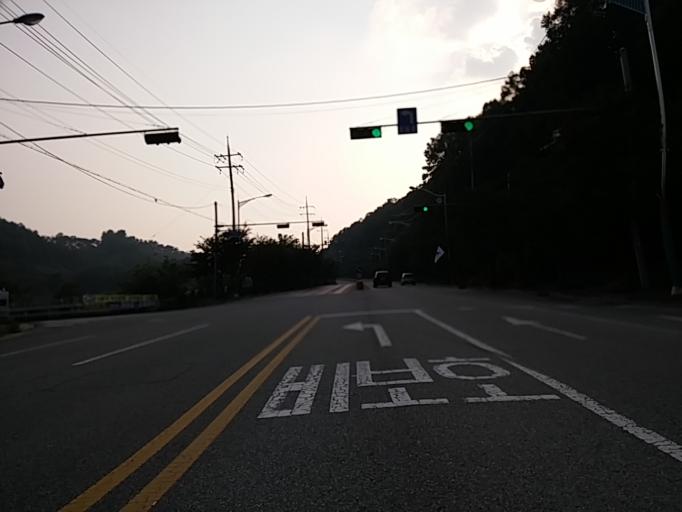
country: KR
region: Daejeon
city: Daejeon
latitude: 36.3390
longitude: 127.4900
